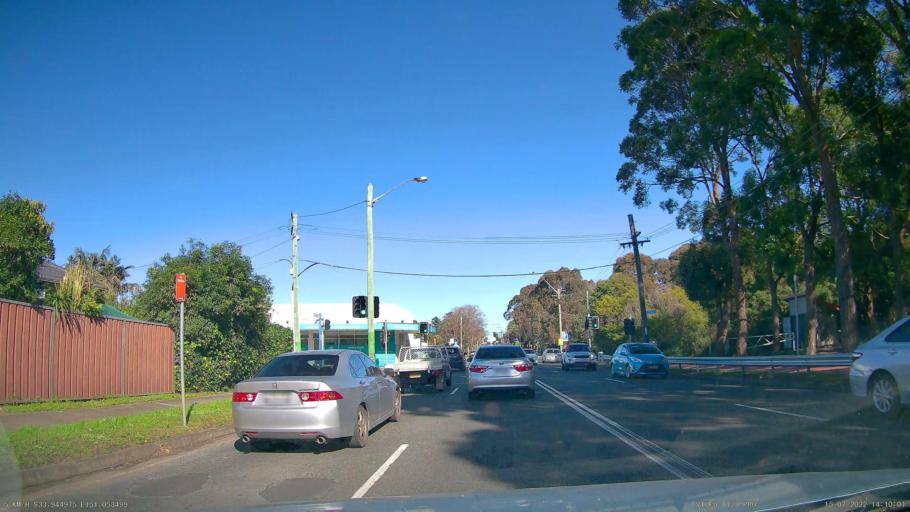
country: AU
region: New South Wales
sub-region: Hurstville
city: Peakhurst
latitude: -33.9451
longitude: 151.0535
